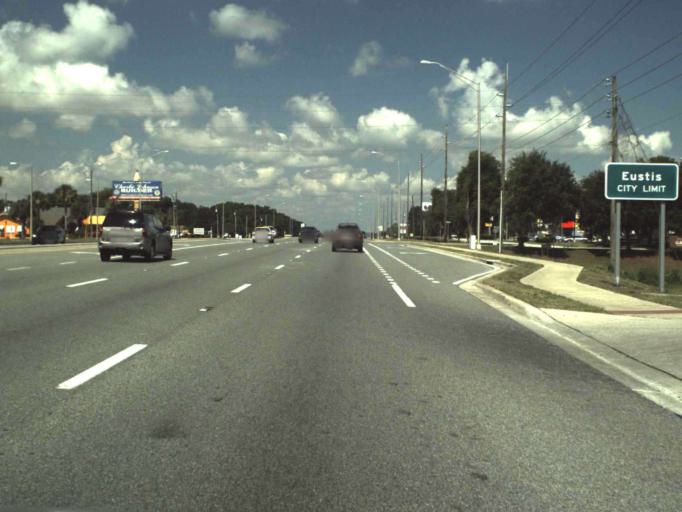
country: US
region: Florida
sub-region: Lake County
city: Mount Dora
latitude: 28.8242
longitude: -81.6456
